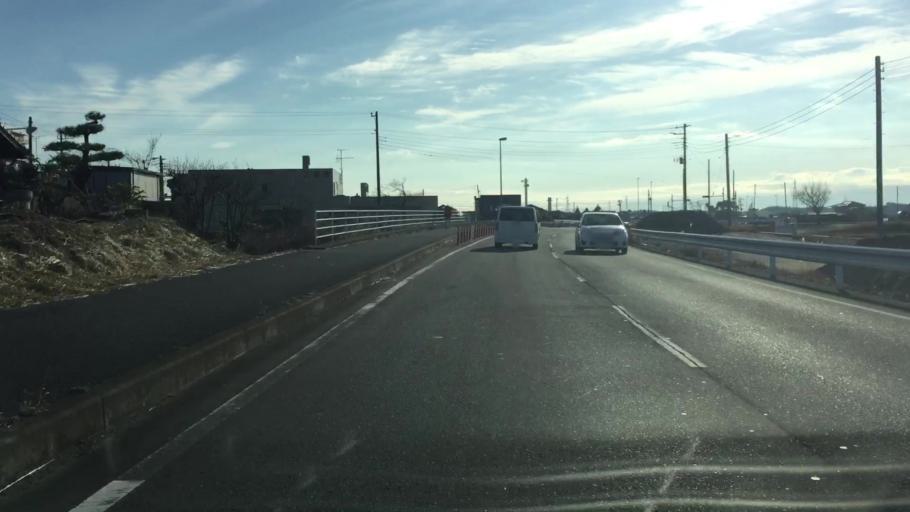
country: JP
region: Ibaraki
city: Toride
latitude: 35.8491
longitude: 140.1292
